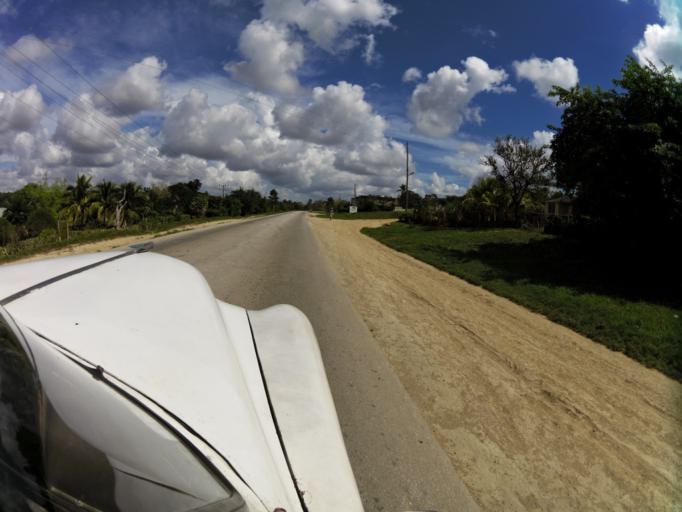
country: CU
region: Holguin
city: Cacocum
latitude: 20.8662
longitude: -76.4364
